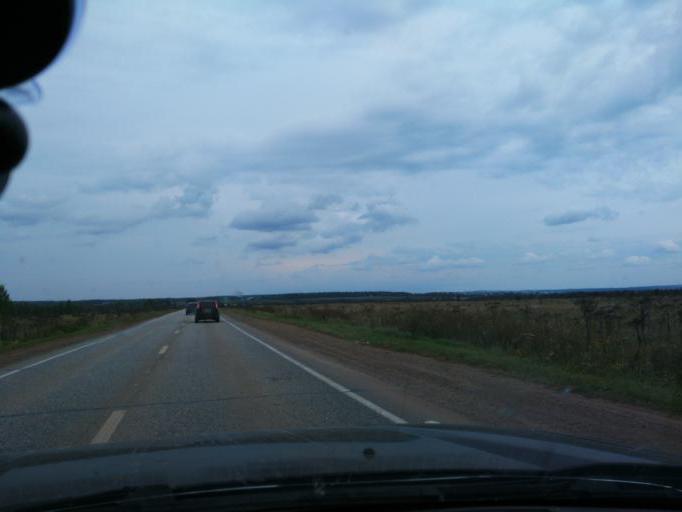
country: RU
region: Perm
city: Chernushka
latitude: 56.5059
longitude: 55.9939
